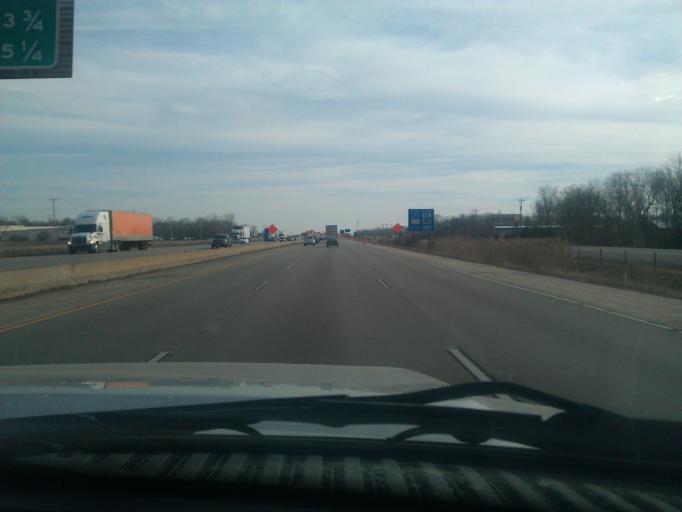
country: US
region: Wisconsin
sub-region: Racine County
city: Franksville
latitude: 42.7505
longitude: -87.9542
